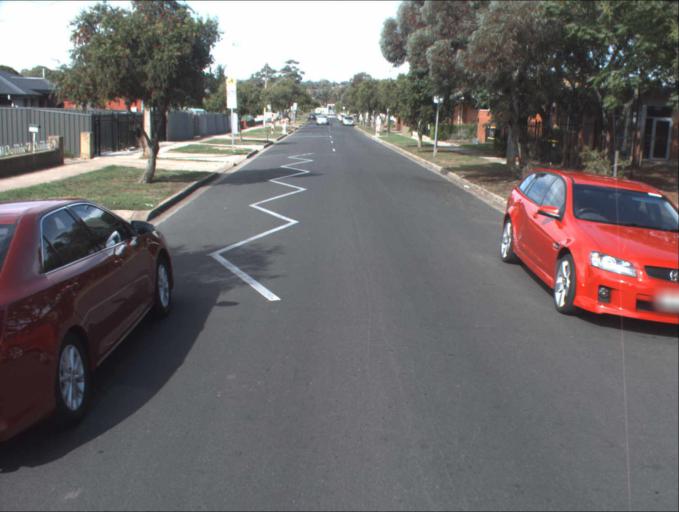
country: AU
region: South Australia
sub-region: Port Adelaide Enfield
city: Blair Athol
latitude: -34.8609
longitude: 138.5871
